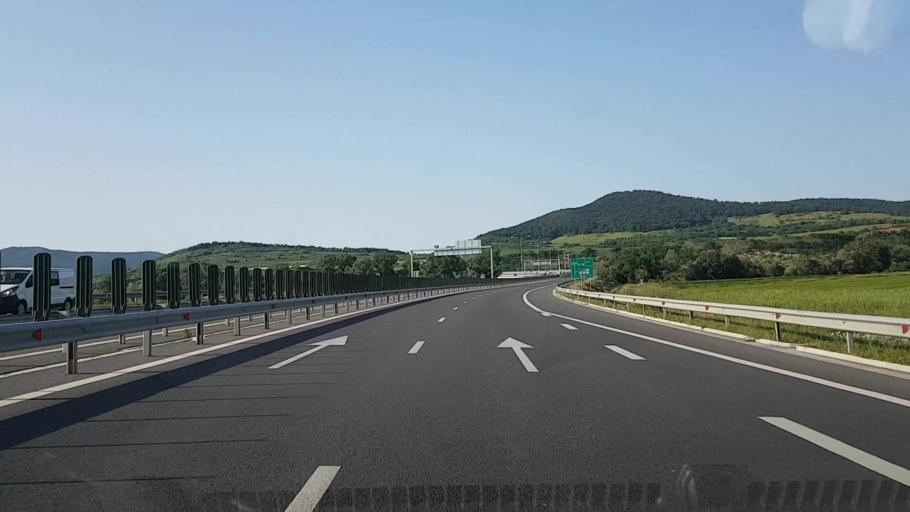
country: RO
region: Alba
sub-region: Municipiul Aiud
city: Aiud
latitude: 46.3327
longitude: 23.7297
